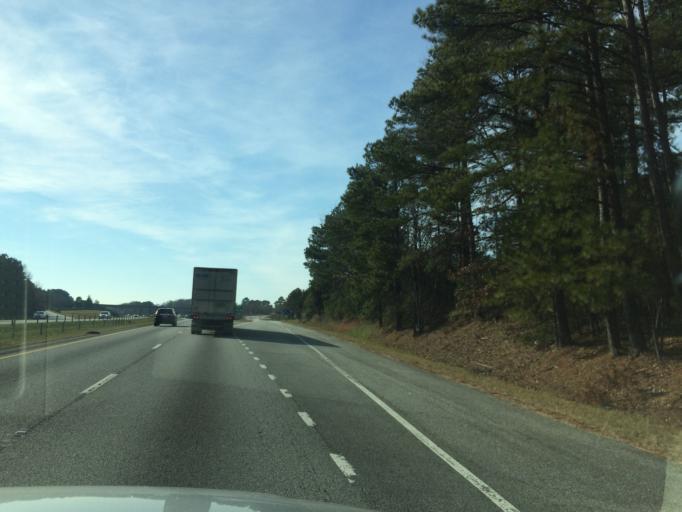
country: US
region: South Carolina
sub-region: Anderson County
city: Centerville
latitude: 34.5492
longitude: -82.8022
